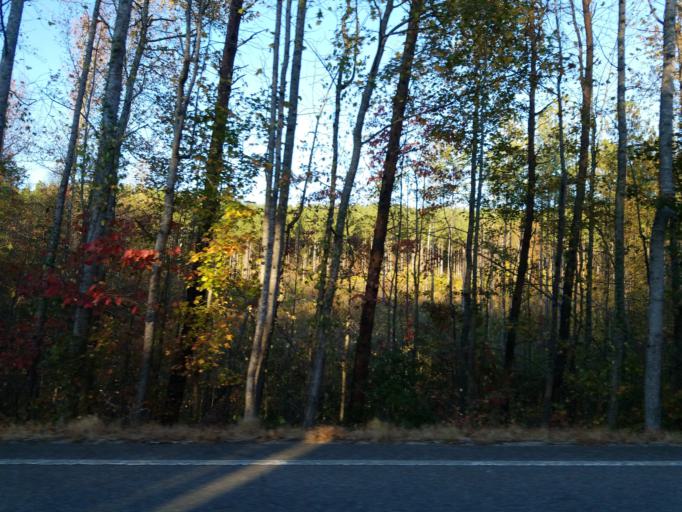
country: US
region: Georgia
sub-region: Dawson County
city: Dawsonville
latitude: 34.5414
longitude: -84.2183
